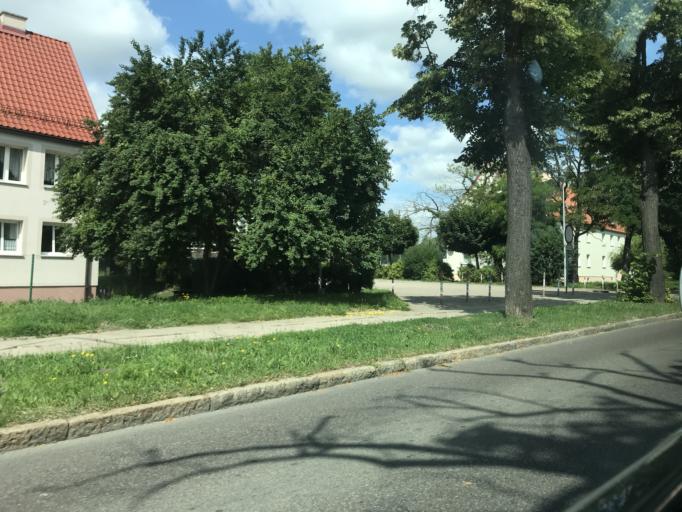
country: PL
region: Warmian-Masurian Voivodeship
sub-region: Powiat elblaski
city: Elblag
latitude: 54.1657
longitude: 19.4248
